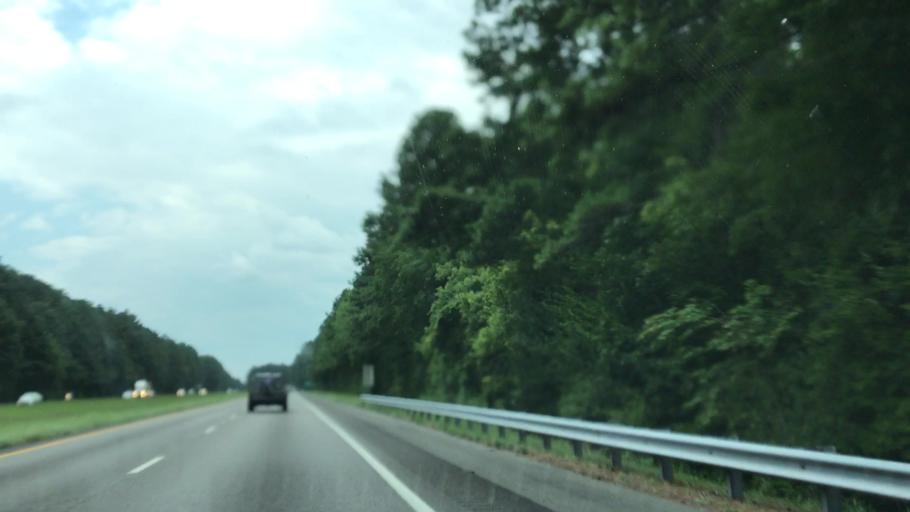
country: US
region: South Carolina
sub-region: Richland County
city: Blythewood
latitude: 34.2697
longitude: -80.9980
